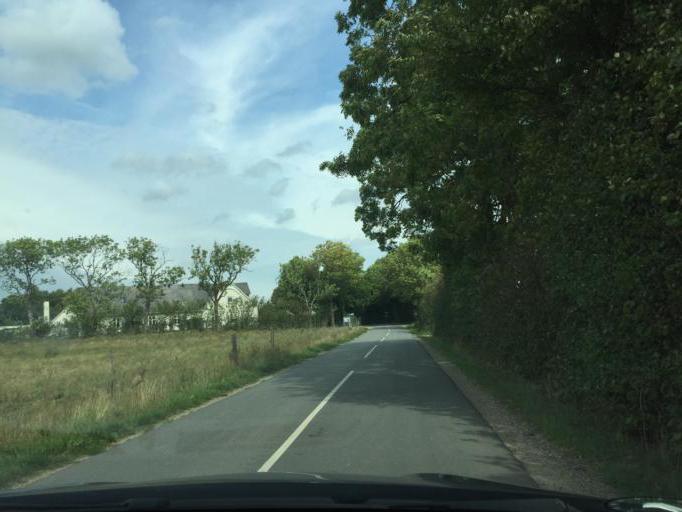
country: DK
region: South Denmark
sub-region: Assens Kommune
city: Tommerup Stationsby
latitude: 55.3845
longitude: 10.1772
